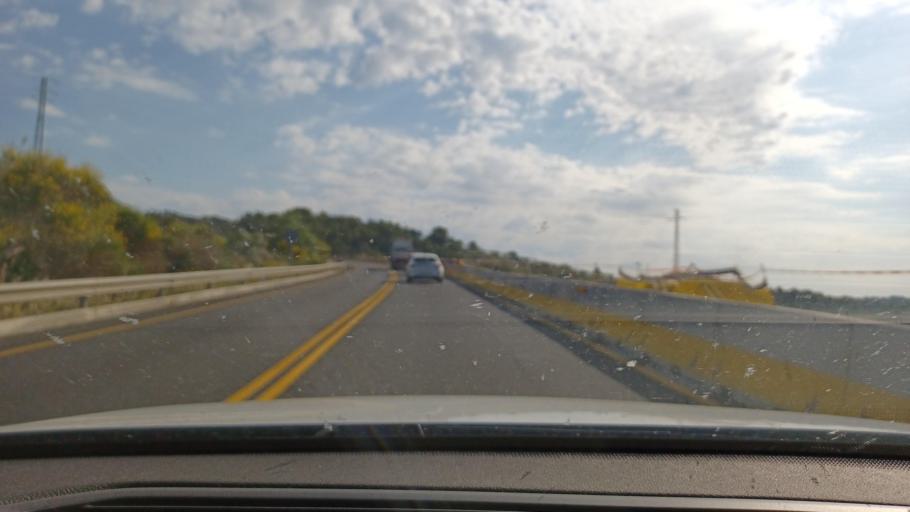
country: ES
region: Catalonia
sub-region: Provincia de Barcelona
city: Sant Pere de Riudebitlles
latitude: 41.4593
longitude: 1.6939
